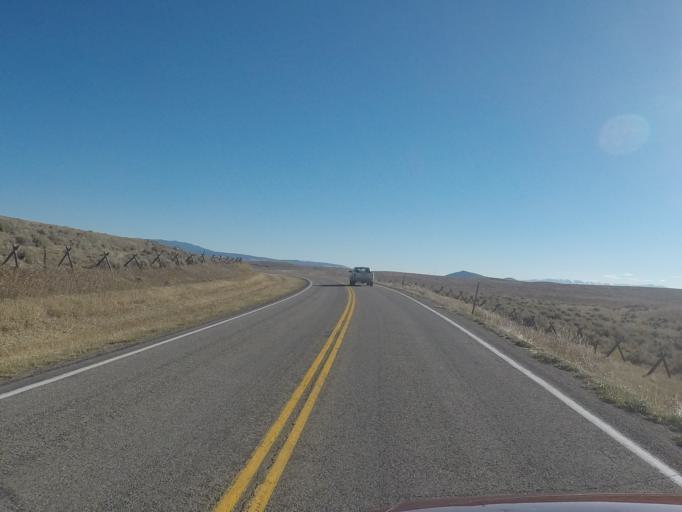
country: US
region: Montana
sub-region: Meagher County
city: White Sulphur Springs
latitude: 46.3553
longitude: -111.0249
